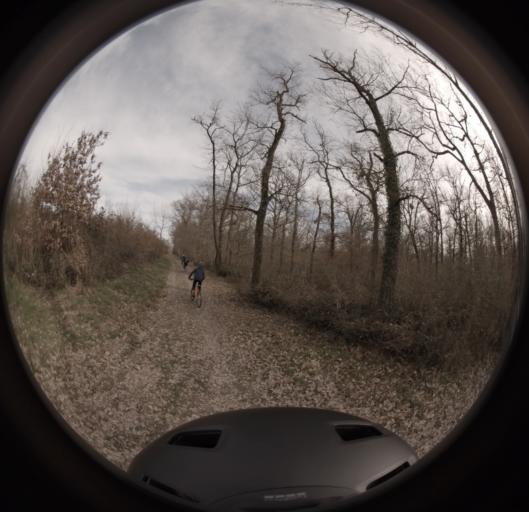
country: FR
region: Midi-Pyrenees
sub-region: Departement du Tarn-et-Garonne
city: Montech
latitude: 43.9567
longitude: 1.2588
